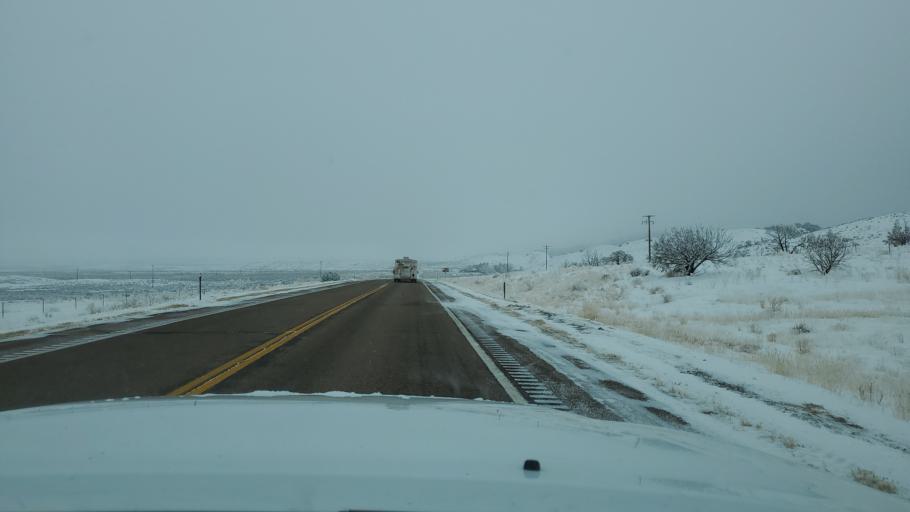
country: US
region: Colorado
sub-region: Rio Blanco County
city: Rangely
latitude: 40.2427
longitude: -108.9621
